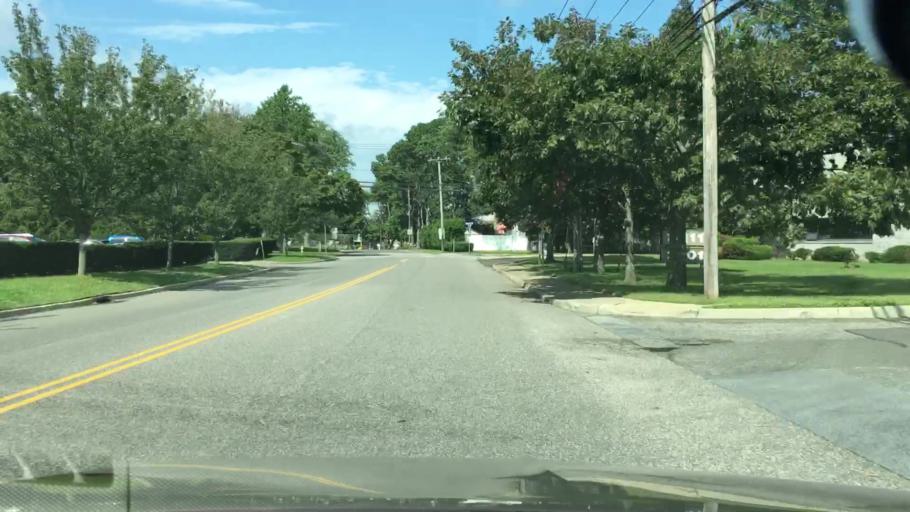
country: US
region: New York
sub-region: Suffolk County
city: Islandia
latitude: 40.7970
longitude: -73.1390
